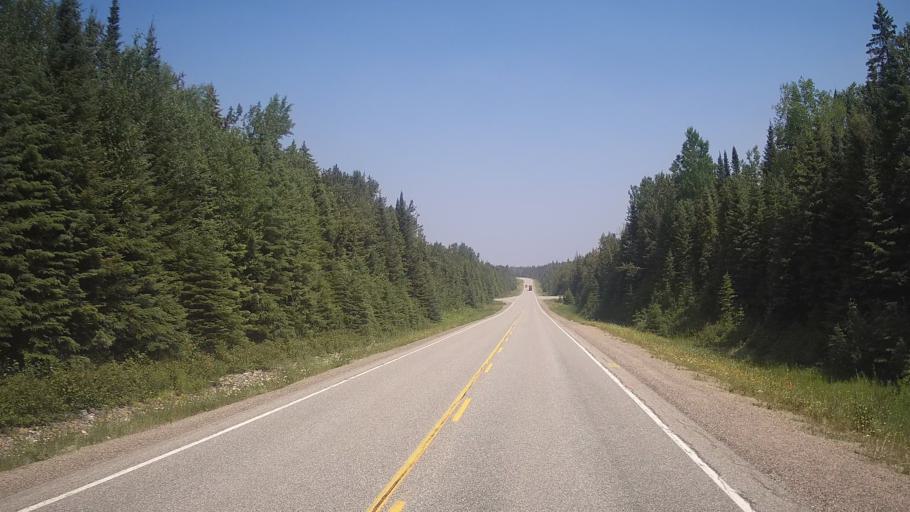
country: CA
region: Ontario
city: Timmins
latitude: 48.0906
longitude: -81.5943
